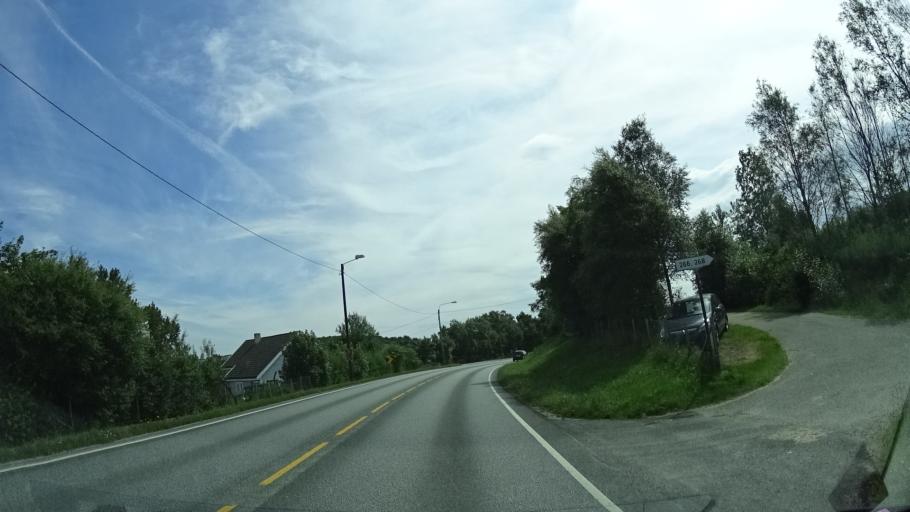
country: NO
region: Rogaland
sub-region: Randaberg
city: Randaberg
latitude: 58.9888
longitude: 5.6632
